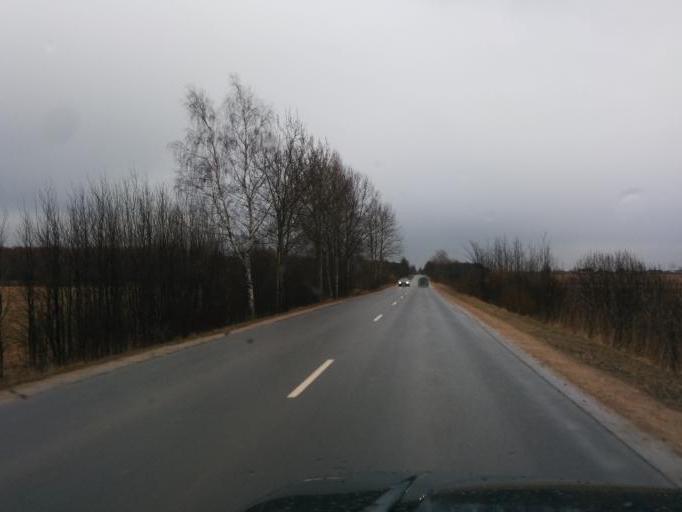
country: LV
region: Kekava
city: Balozi
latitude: 56.8945
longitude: 24.1563
